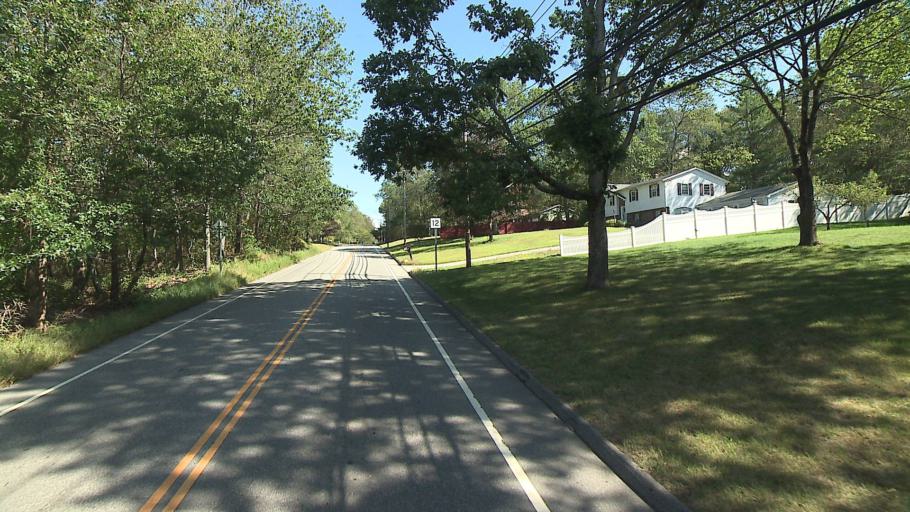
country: US
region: Connecticut
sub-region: Windham County
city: East Brooklyn
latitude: 41.7703
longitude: -71.8981
